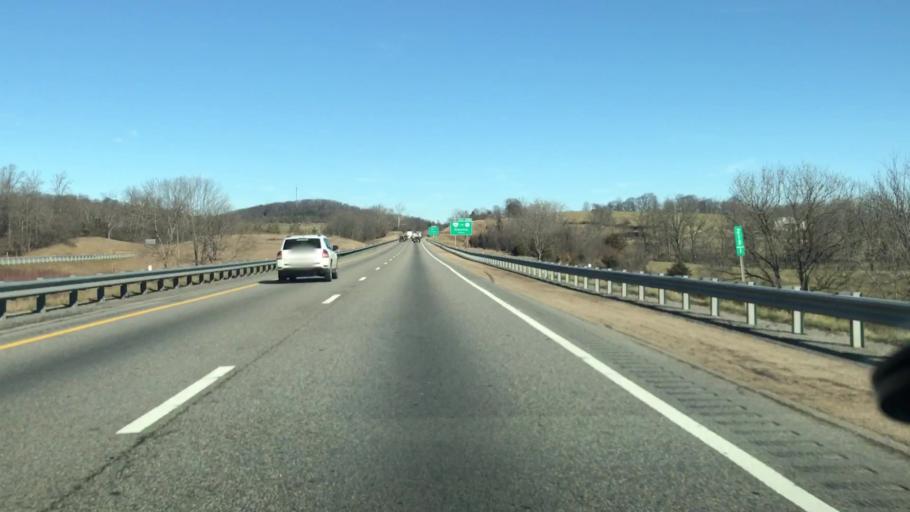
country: US
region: Virginia
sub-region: Augusta County
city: Jolivue
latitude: 38.0899
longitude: -79.0764
